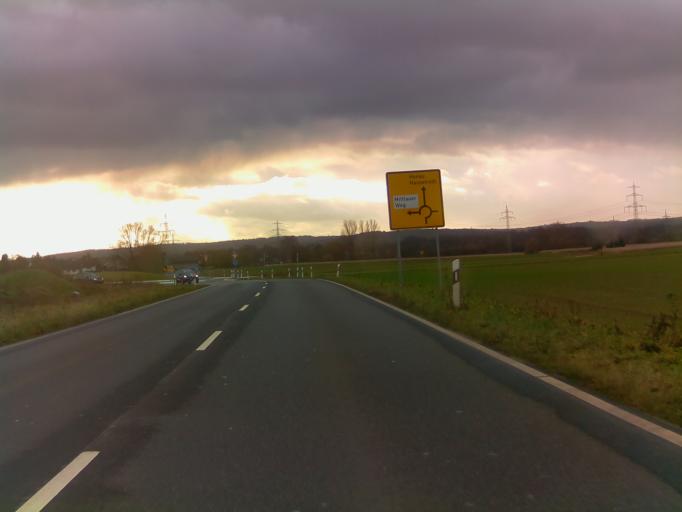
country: DE
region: Hesse
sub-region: Regierungsbezirk Darmstadt
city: Gelnhausen
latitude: 50.1797
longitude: 9.1323
